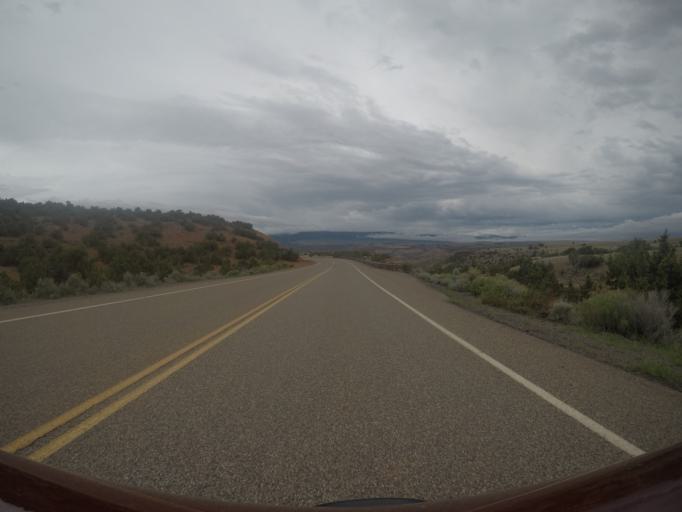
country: US
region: Wyoming
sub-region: Big Horn County
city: Lovell
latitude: 45.1017
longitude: -108.2411
